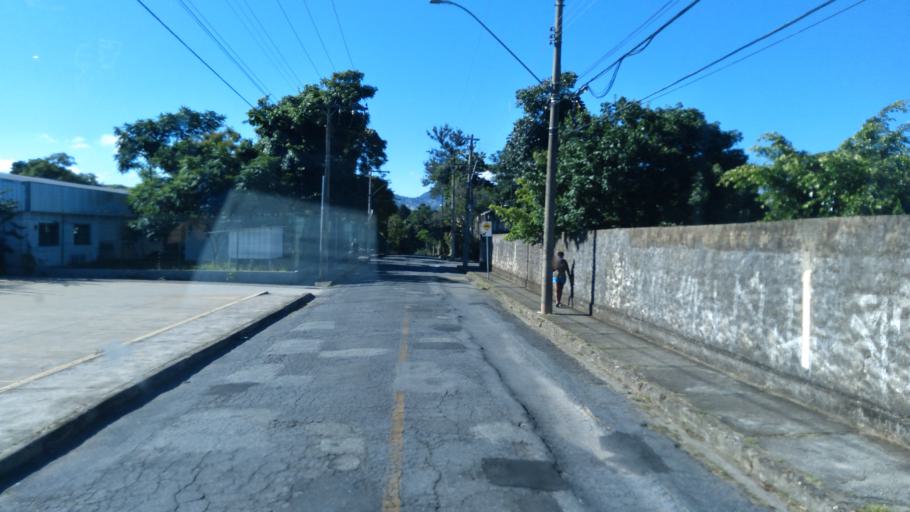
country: BR
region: Minas Gerais
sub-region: Belo Horizonte
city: Belo Horizonte
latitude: -19.8865
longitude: -43.9147
